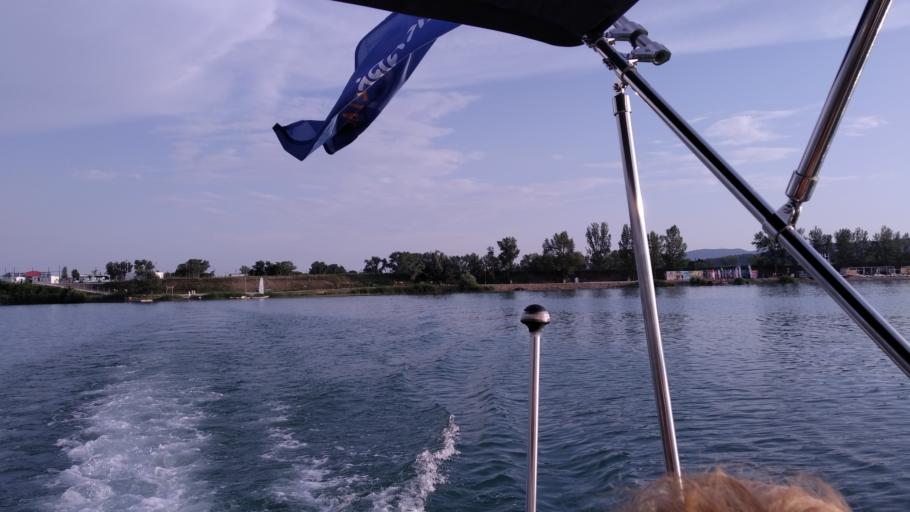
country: HU
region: Pest
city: Budakalasz
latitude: 47.6245
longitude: 19.0755
